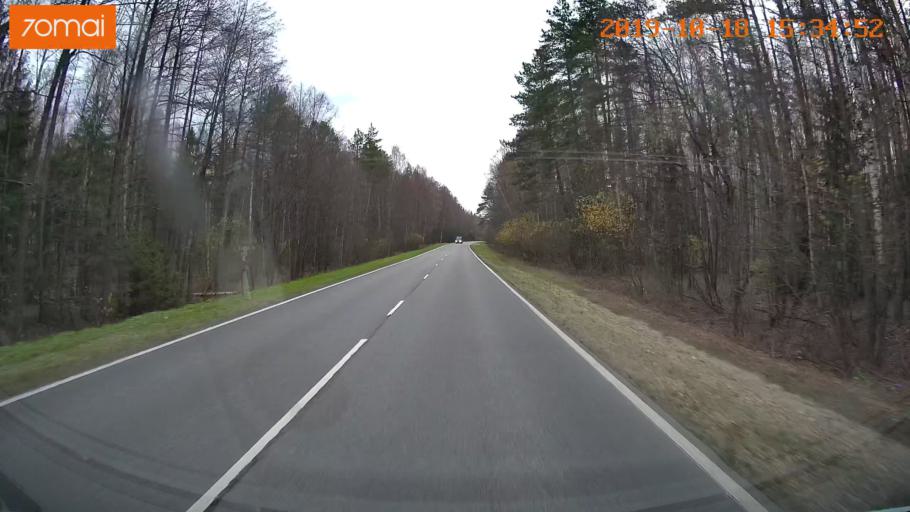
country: RU
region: Vladimir
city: Anopino
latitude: 55.8600
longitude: 40.6371
